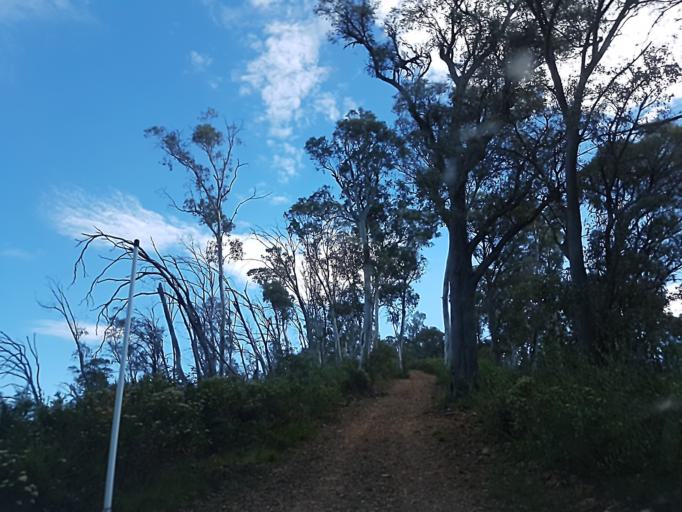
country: AU
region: Victoria
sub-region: Alpine
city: Mount Beauty
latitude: -36.9112
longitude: 147.0137
